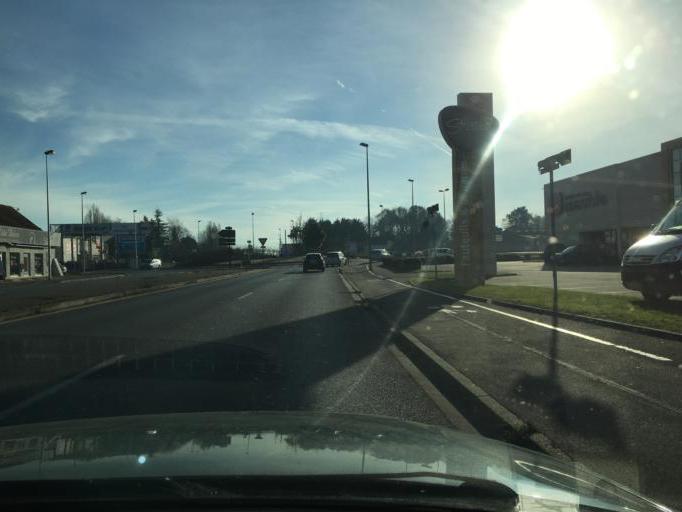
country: FR
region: Centre
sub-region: Departement du Loiret
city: Saran
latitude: 47.9579
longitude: 1.8901
